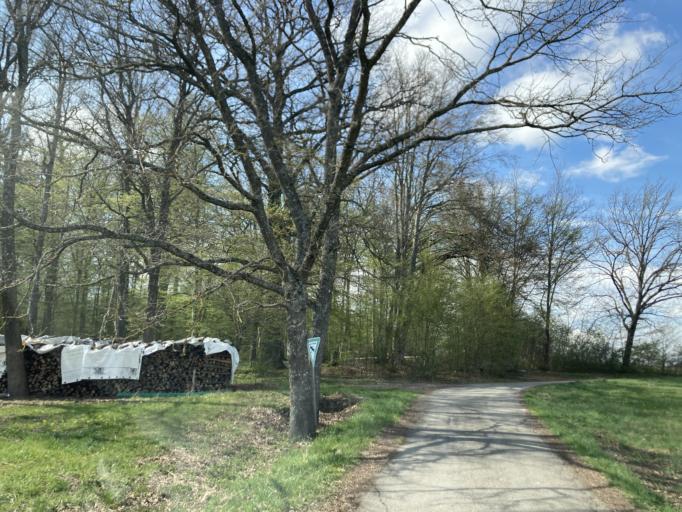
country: DE
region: Baden-Wuerttemberg
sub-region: Tuebingen Region
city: Dettenhausen
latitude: 48.6032
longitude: 9.0897
